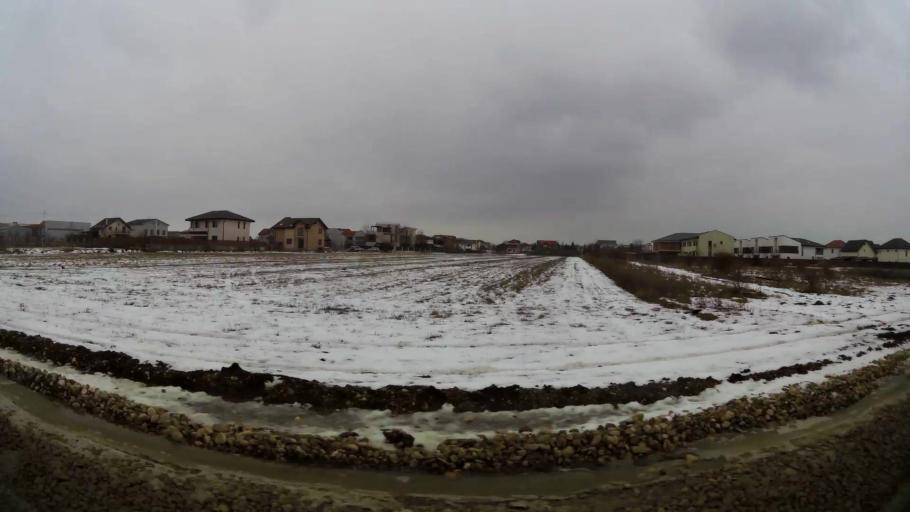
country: RO
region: Ilfov
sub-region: Comuna Otopeni
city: Otopeni
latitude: 44.5453
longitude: 26.0858
